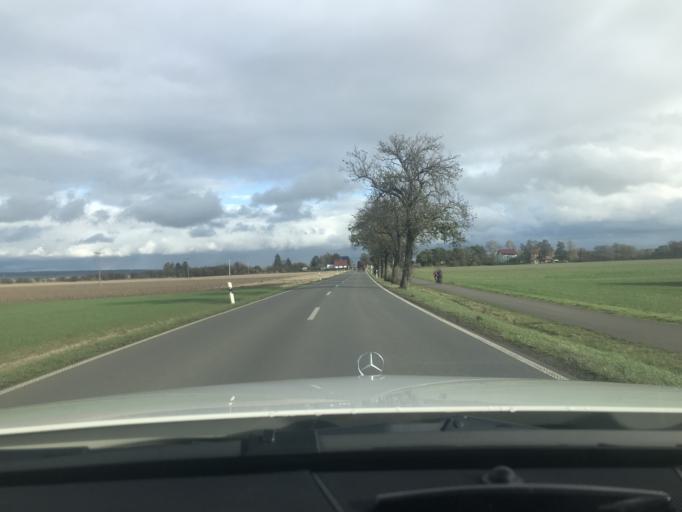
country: DE
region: Thuringia
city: Warza
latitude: 50.9990
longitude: 10.7016
